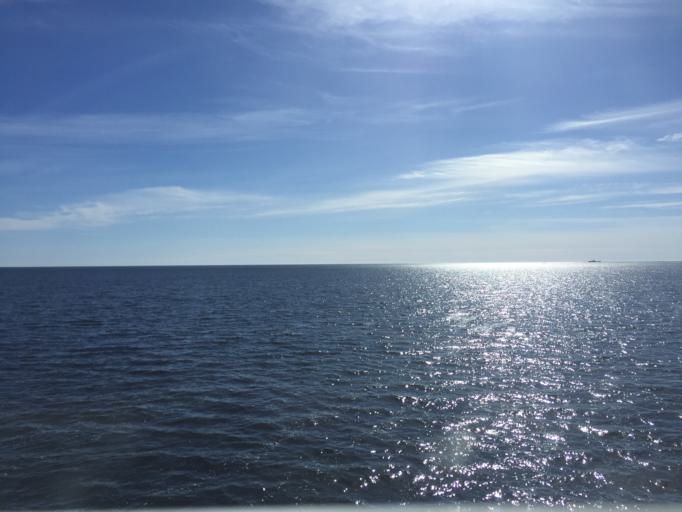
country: EE
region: Laeaene
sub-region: Haapsalu linn
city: Haapsalu
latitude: 58.5759
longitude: 23.4671
